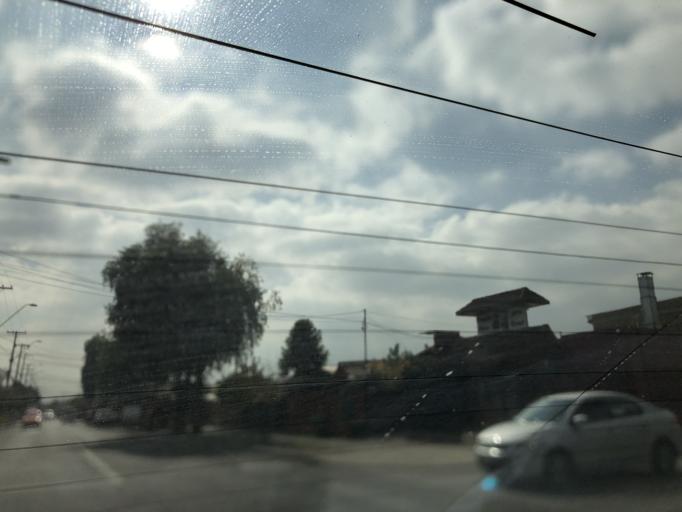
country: CL
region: Santiago Metropolitan
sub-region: Provincia de Cordillera
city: Puente Alto
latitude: -33.5911
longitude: -70.5910
